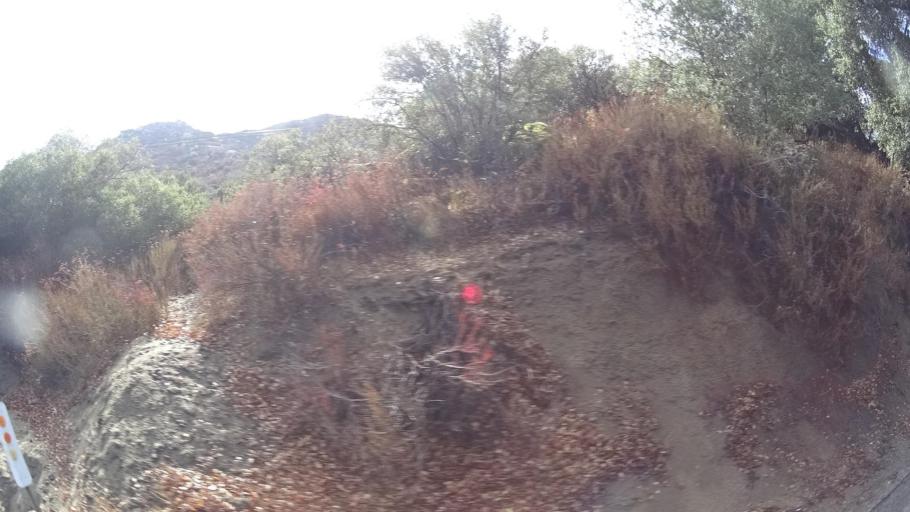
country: US
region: California
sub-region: San Diego County
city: Campo
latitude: 32.6006
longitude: -116.4914
